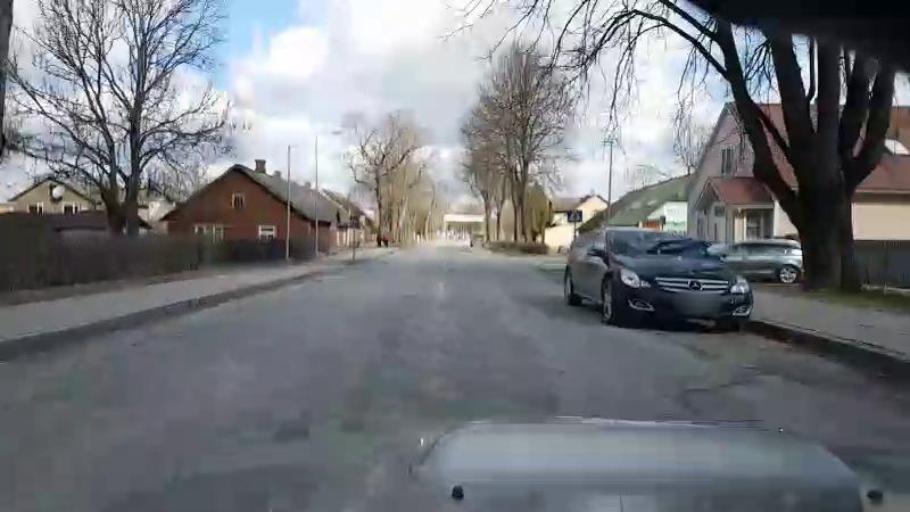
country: EE
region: Jaervamaa
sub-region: Paide linn
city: Paide
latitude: 58.8901
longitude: 25.5691
